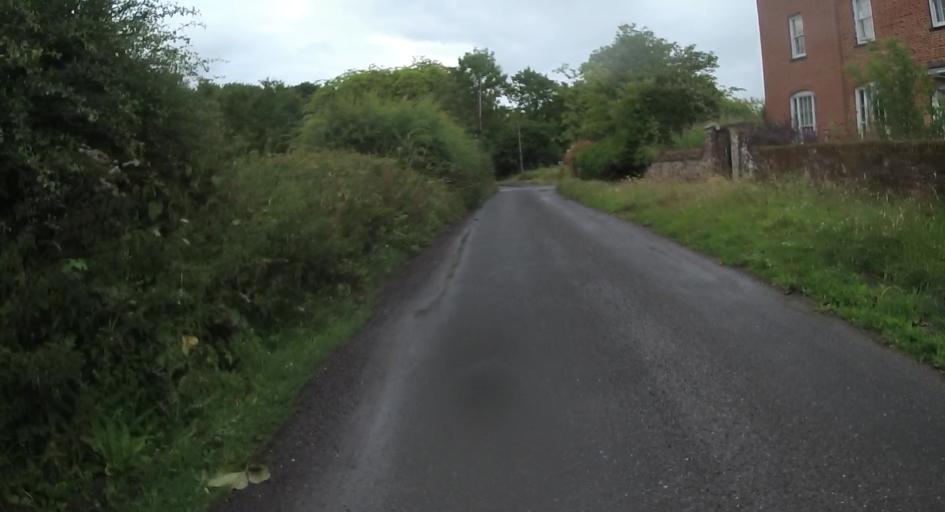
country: GB
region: England
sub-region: Hampshire
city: Long Sutton
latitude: 51.2126
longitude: -0.9114
